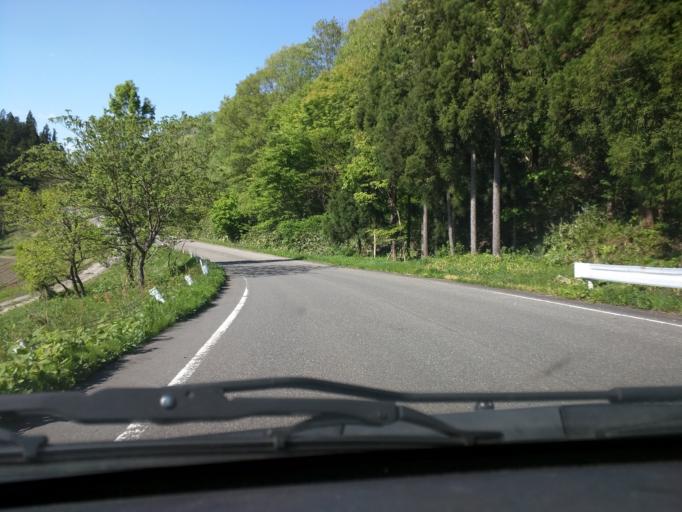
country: JP
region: Fukushima
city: Kitakata
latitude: 37.5677
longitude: 139.6349
